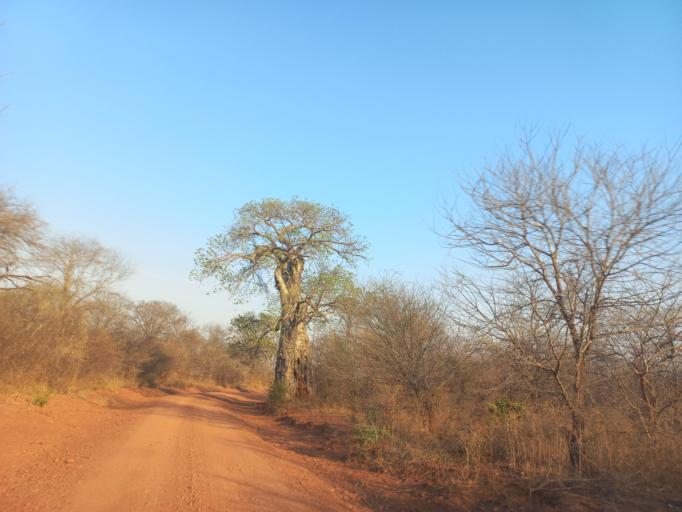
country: ZM
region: Lusaka
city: Luangwa
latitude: -15.4466
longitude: 30.3706
